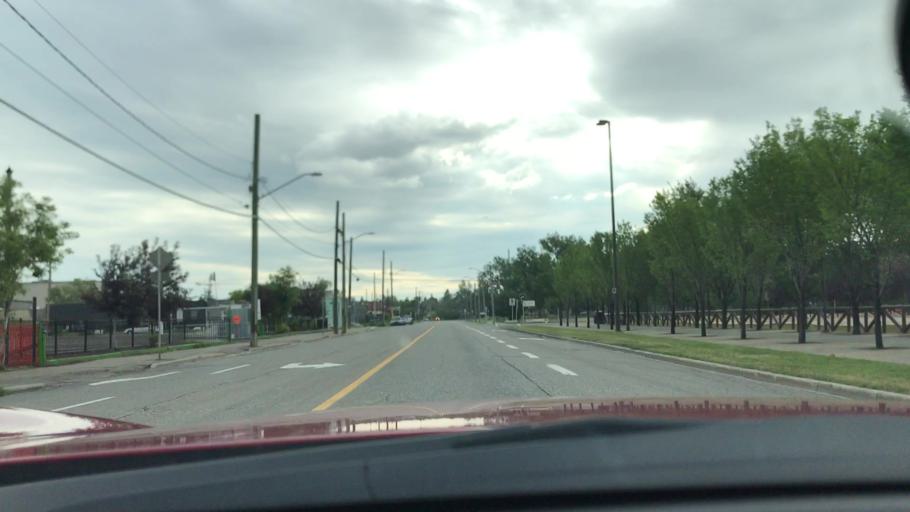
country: CA
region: Alberta
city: Calgary
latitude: 51.0411
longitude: -114.0526
